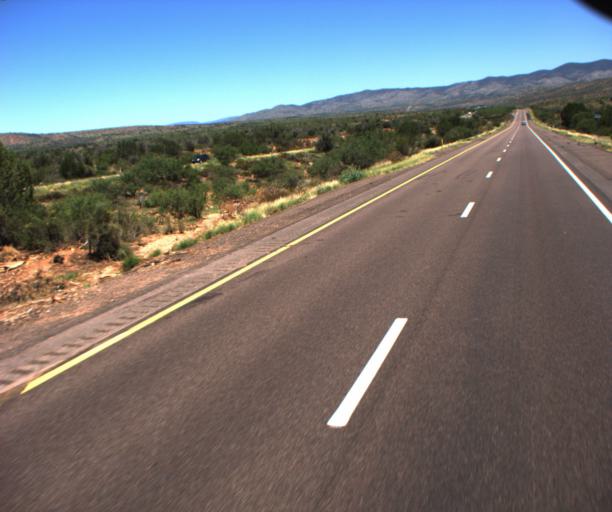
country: US
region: Arizona
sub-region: Gila County
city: Payson
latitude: 34.0680
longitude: -111.3591
